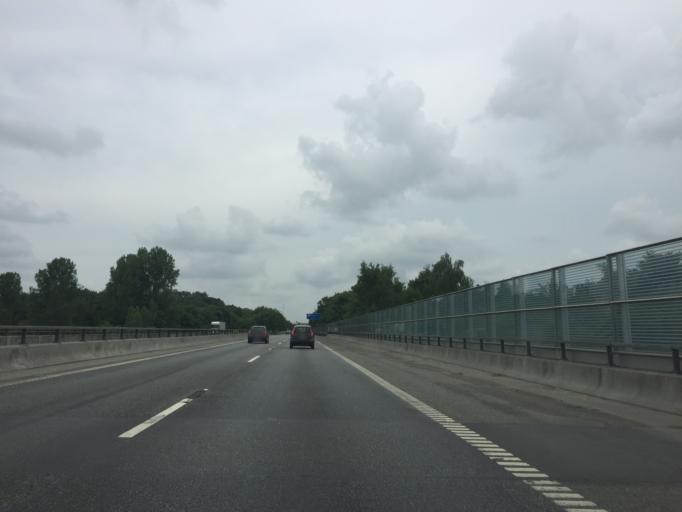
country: DK
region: Capital Region
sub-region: Fureso Kommune
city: Farum
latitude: 55.8054
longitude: 12.3807
